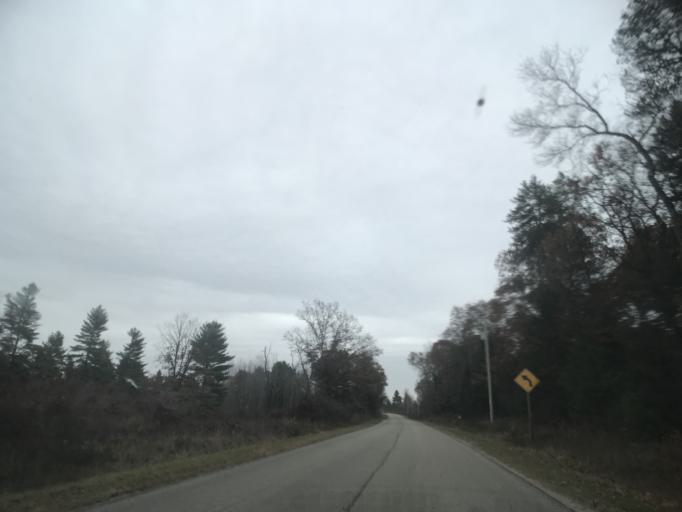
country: US
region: Wisconsin
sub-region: Oconto County
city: Gillett
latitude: 45.3017
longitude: -88.2630
